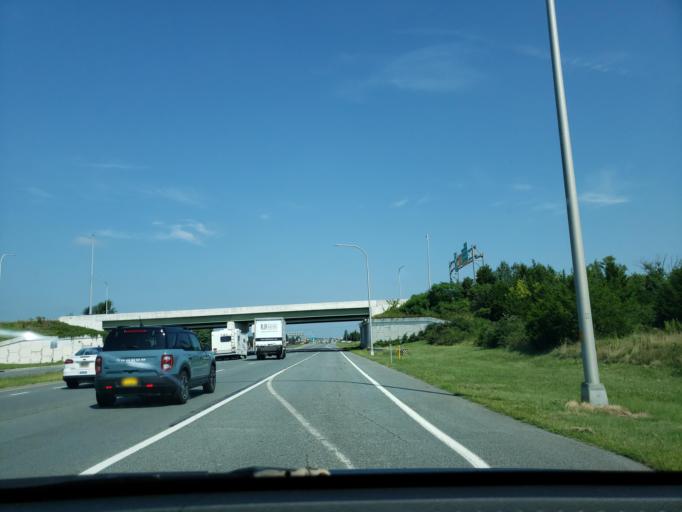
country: US
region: Delaware
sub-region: Kent County
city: Dover
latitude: 39.1456
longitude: -75.4998
